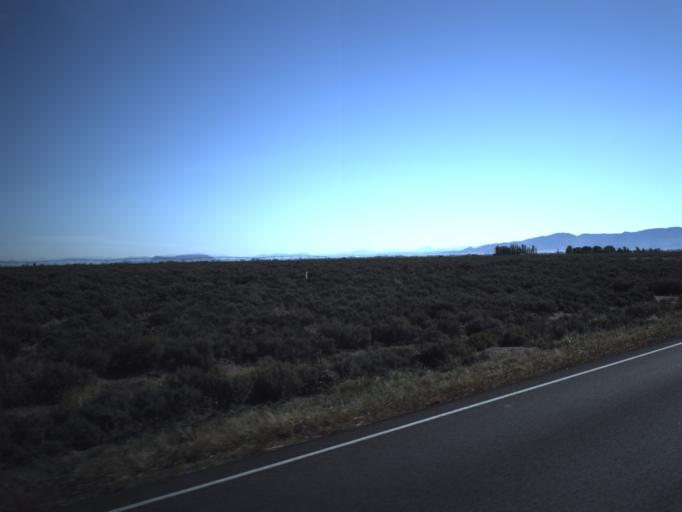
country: US
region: Utah
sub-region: Washington County
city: Enterprise
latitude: 37.7531
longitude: -113.7786
